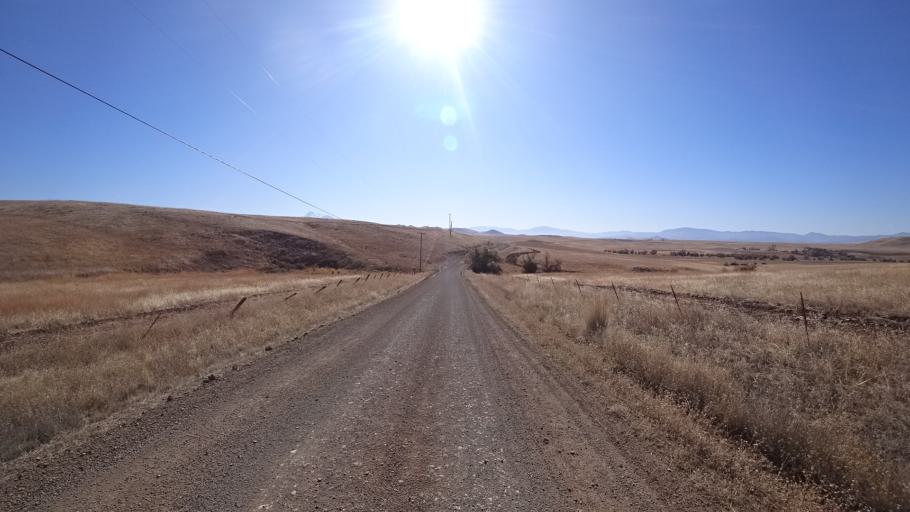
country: US
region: California
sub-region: Siskiyou County
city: Montague
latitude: 41.8329
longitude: -122.4207
